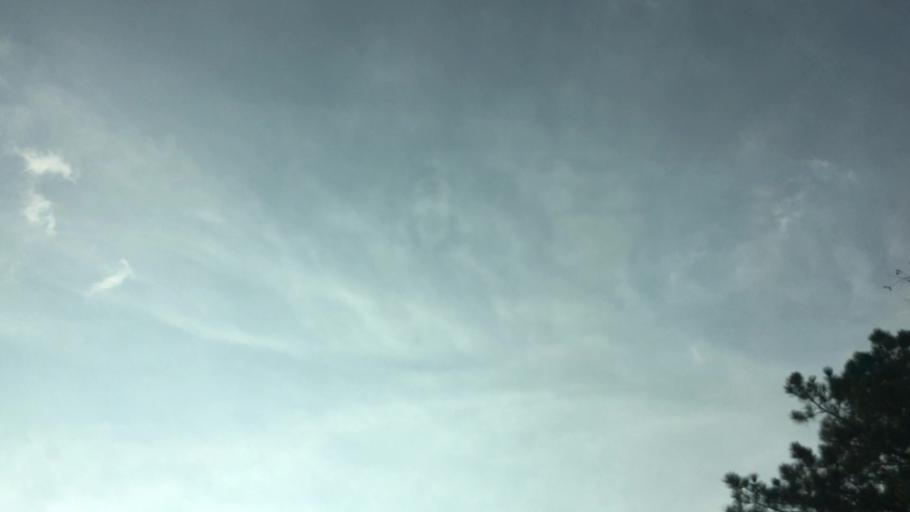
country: US
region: Alabama
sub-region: Bibb County
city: Woodstock
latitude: 33.2178
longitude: -87.1077
